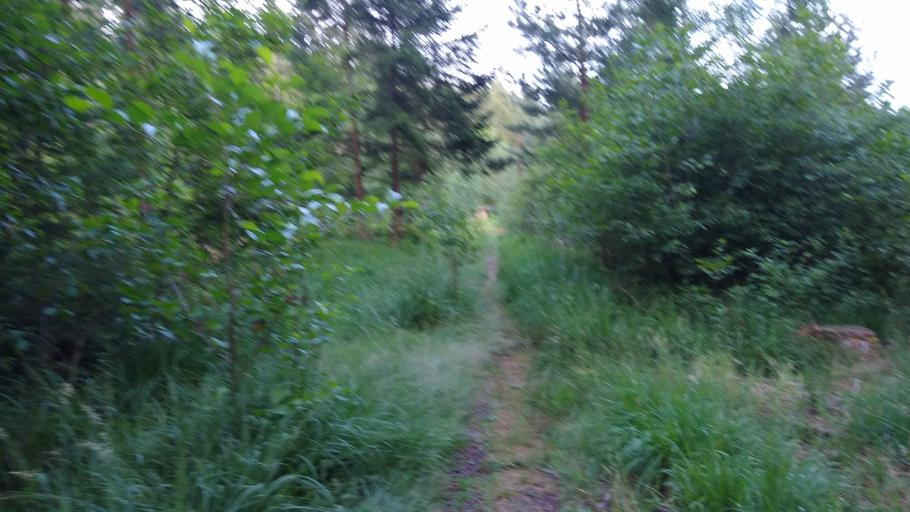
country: DE
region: Hesse
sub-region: Regierungsbezirk Darmstadt
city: Frankisch-Crumbach
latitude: 49.7064
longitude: 8.9143
